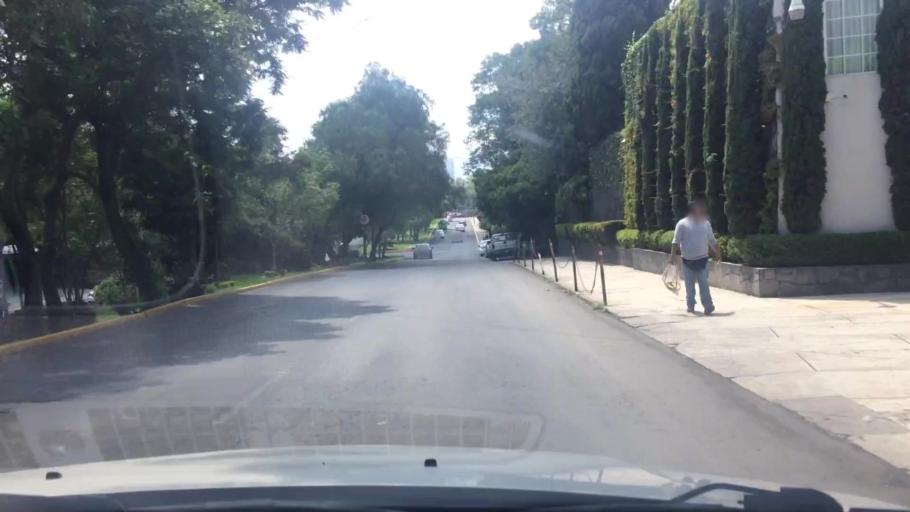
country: MX
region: Mexico City
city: Magdalena Contreras
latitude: 19.3158
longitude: -99.2025
